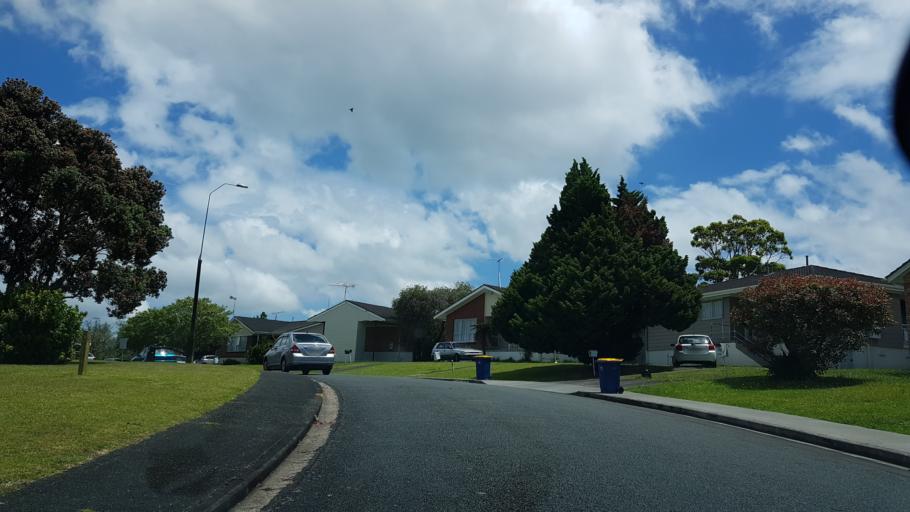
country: NZ
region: Auckland
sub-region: Auckland
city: North Shore
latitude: -36.7976
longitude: 174.7437
